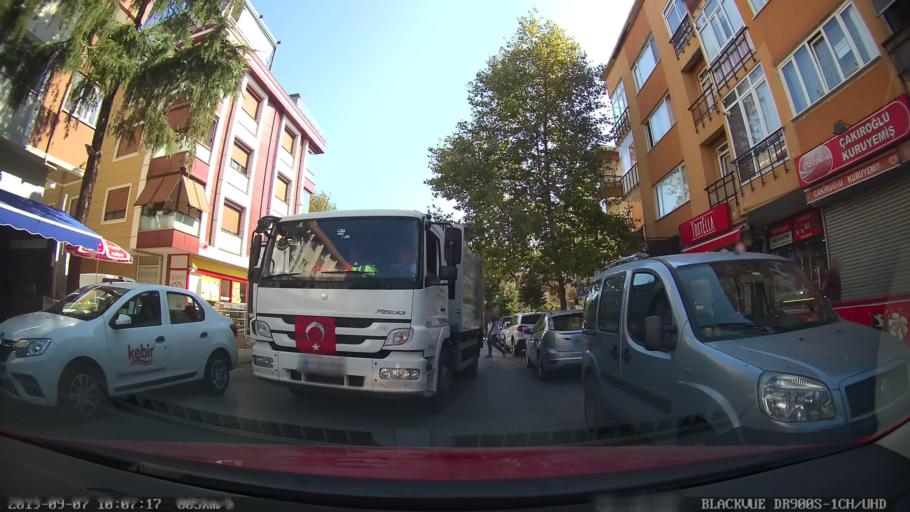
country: TR
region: Istanbul
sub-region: Atasehir
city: Atasehir
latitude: 40.9500
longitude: 29.1117
